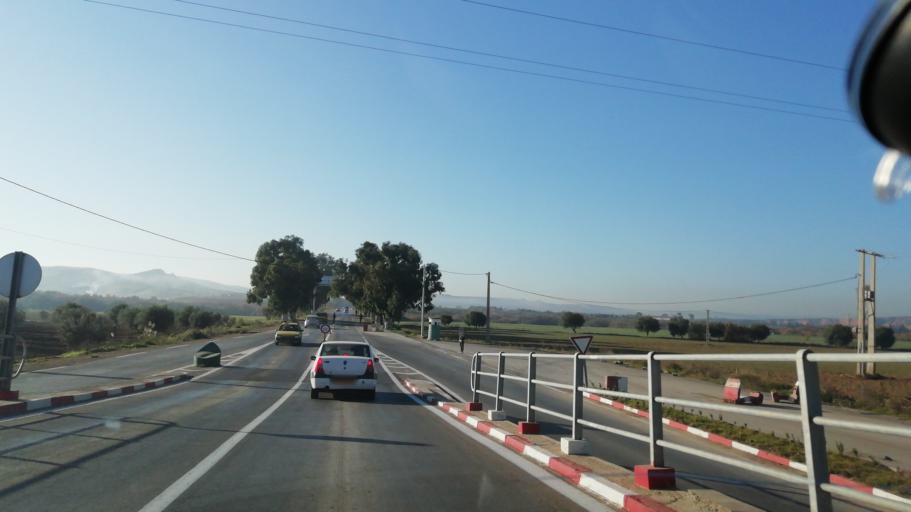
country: DZ
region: Tlemcen
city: Remchi
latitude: 35.0457
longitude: -1.5041
